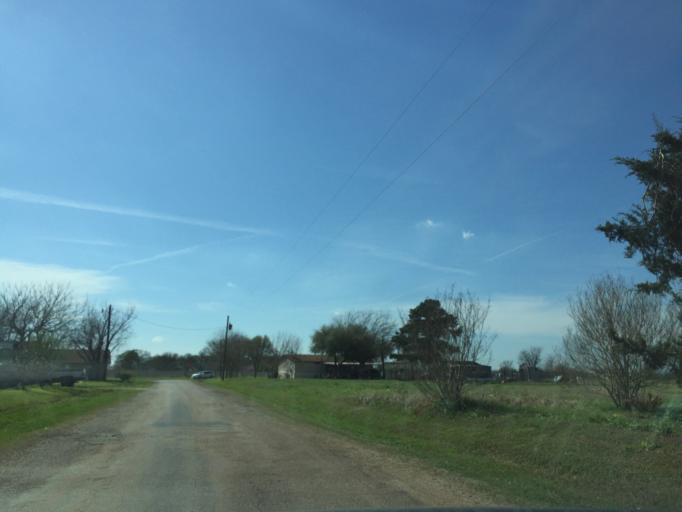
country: US
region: Texas
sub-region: Milam County
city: Thorndale
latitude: 30.5803
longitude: -97.1840
